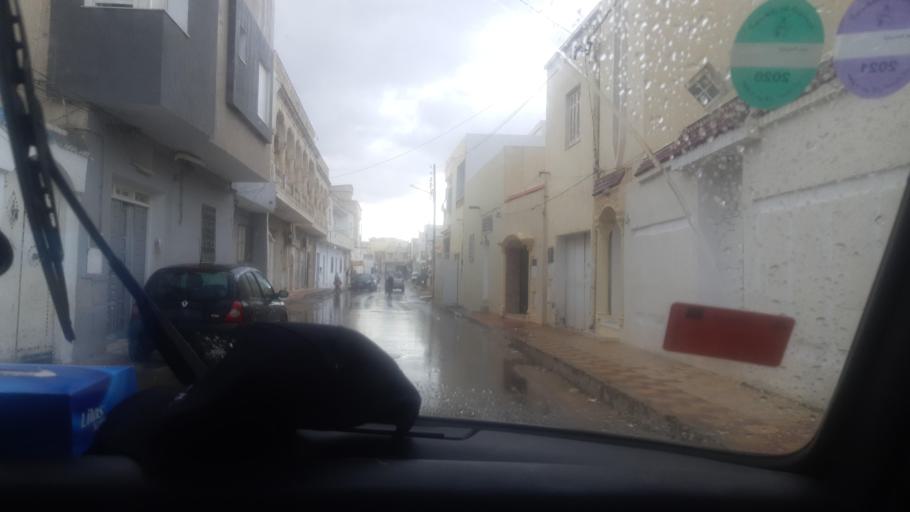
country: TN
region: Susah
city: Akouda
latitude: 35.8719
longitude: 10.5304
